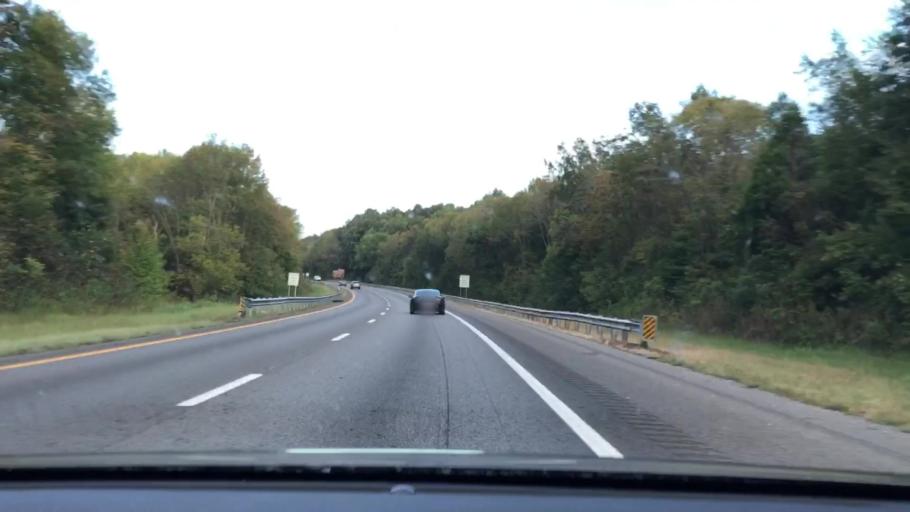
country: US
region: Tennessee
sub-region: Montgomery County
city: Clarksville
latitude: 36.5437
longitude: -87.2377
